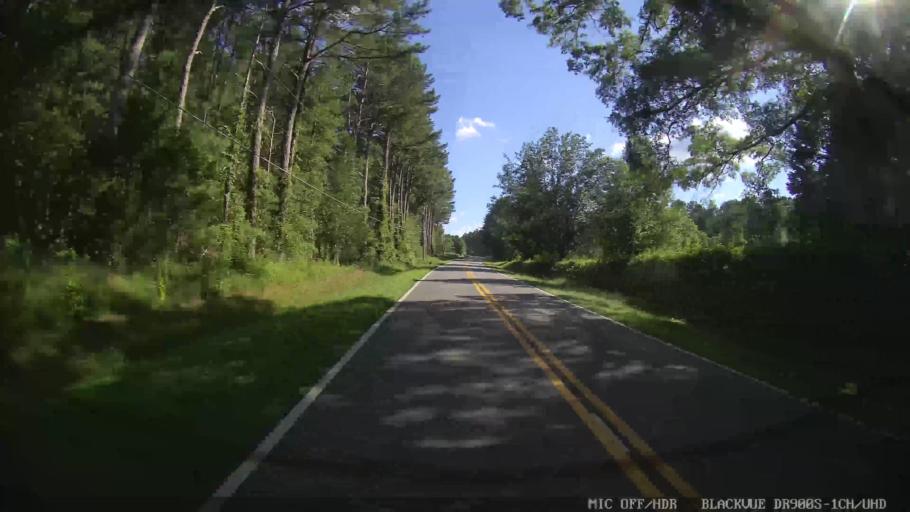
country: US
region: Georgia
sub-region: Bartow County
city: Euharlee
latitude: 34.1685
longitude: -84.9848
